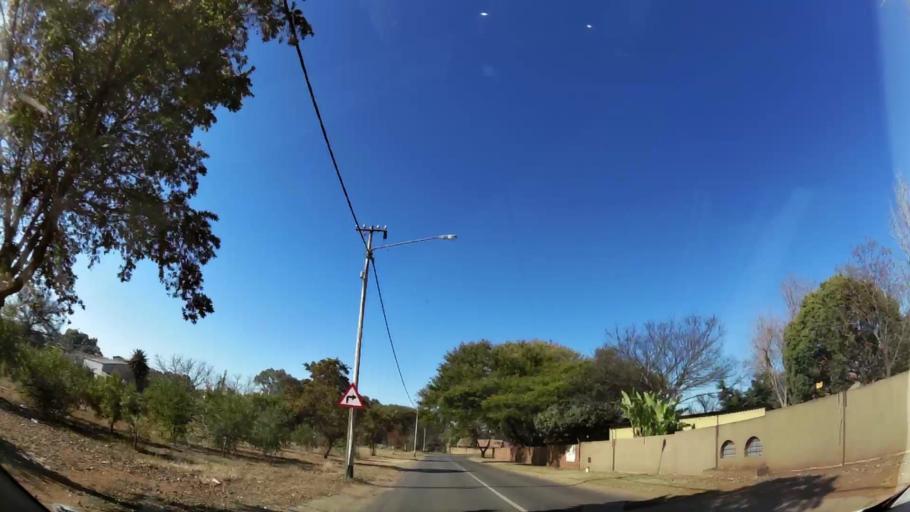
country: ZA
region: Gauteng
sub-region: City of Tshwane Metropolitan Municipality
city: Centurion
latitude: -25.8434
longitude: 28.2130
